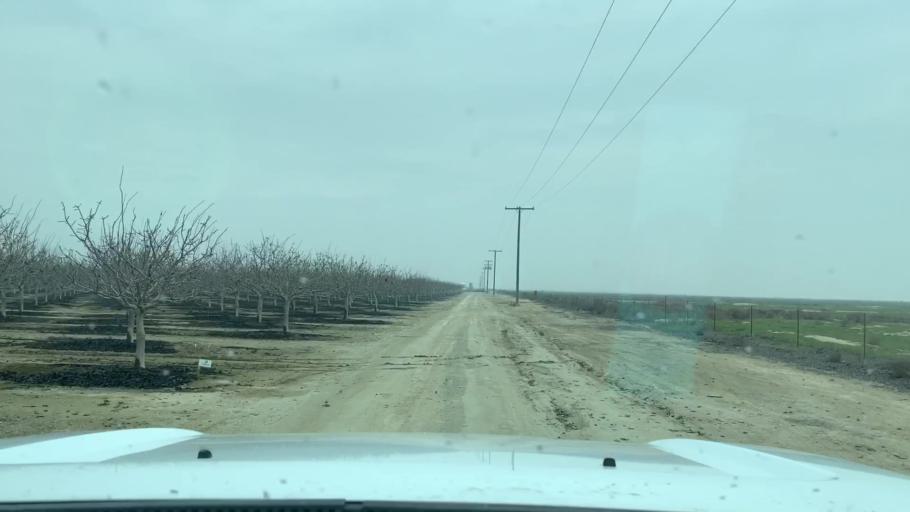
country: US
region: California
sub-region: Tulare County
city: Earlimart
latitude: 35.8379
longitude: -119.3398
